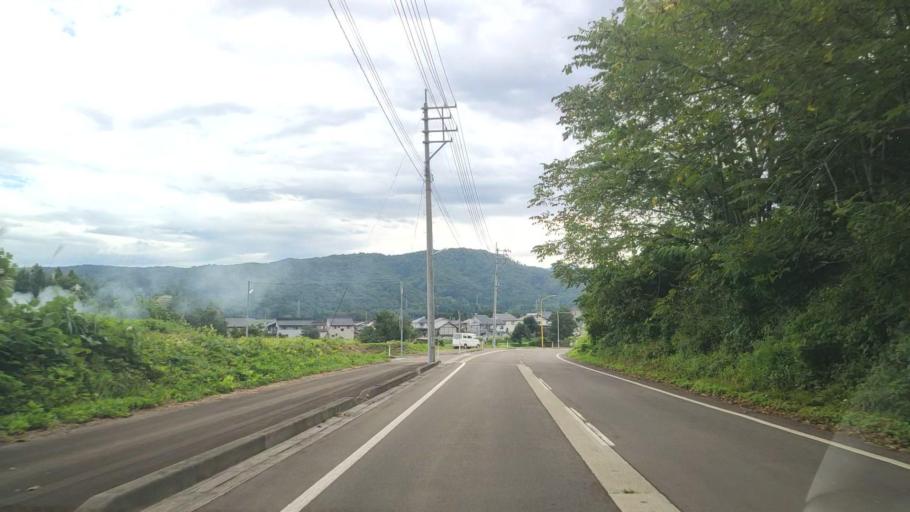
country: JP
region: Niigata
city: Arai
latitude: 37.0121
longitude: 138.2553
